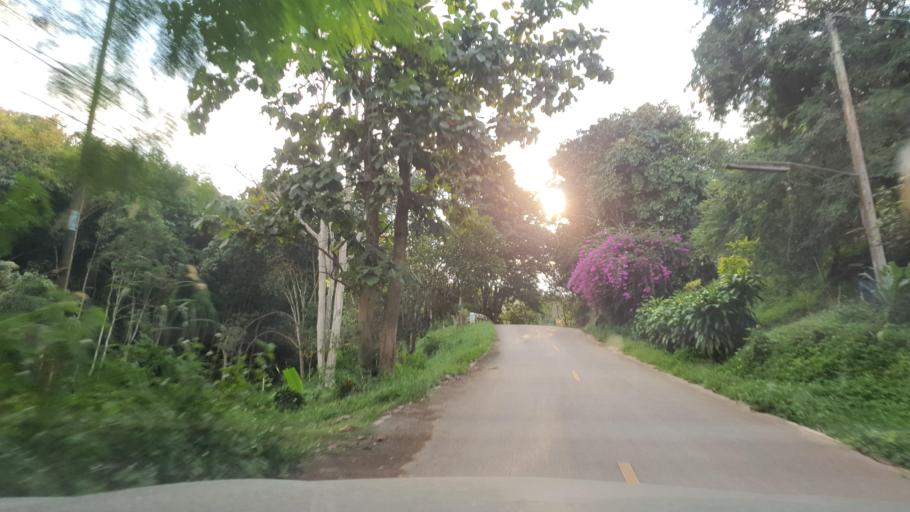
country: TH
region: Chiang Mai
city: Mae On
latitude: 18.8749
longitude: 99.2559
